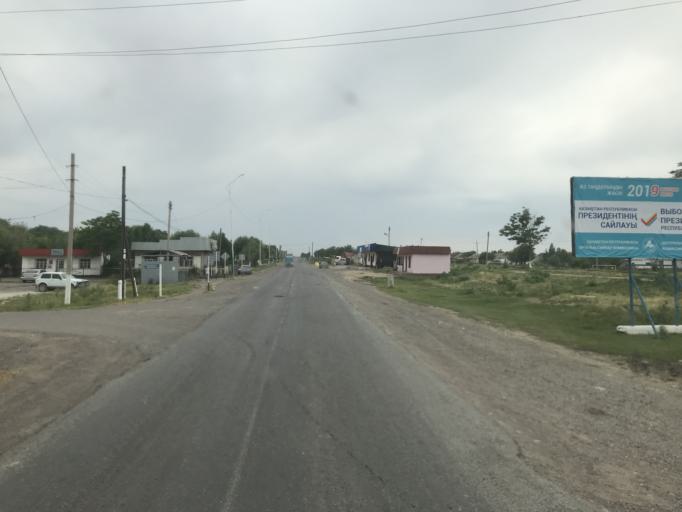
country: KZ
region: Ongtustik Qazaqstan
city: Asykata
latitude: 40.9345
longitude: 68.4097
